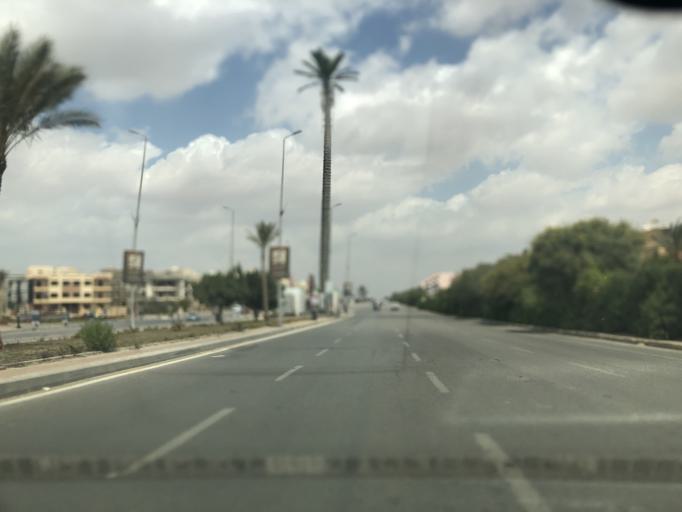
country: EG
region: Muhafazat al Qalyubiyah
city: Al Khankah
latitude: 30.0581
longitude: 31.4751
